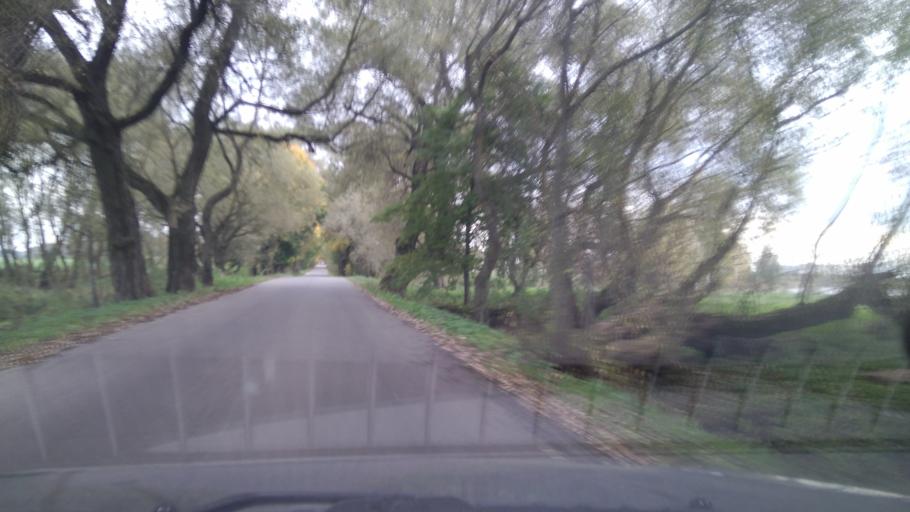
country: BY
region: Minsk
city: Dukora
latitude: 53.6803
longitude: 27.9584
